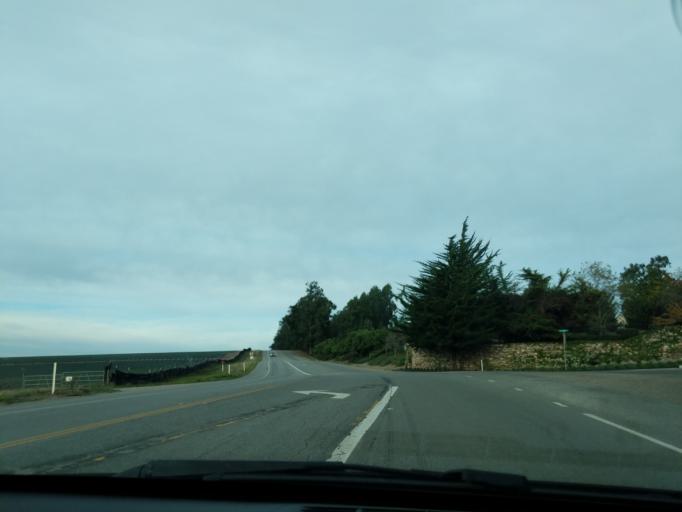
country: US
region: California
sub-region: San Luis Obispo County
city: Callender
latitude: 35.0265
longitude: -120.5612
